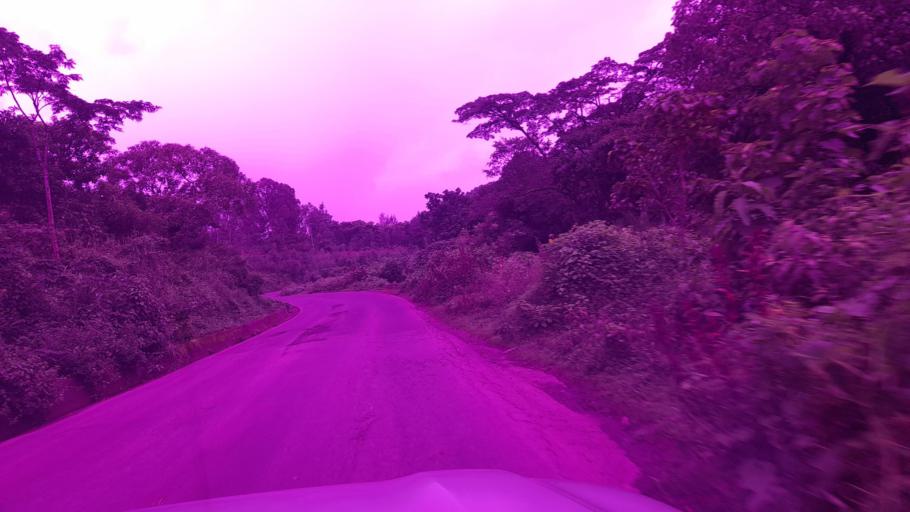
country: ET
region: Oromiya
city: Jima
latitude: 7.6621
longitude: 36.8859
